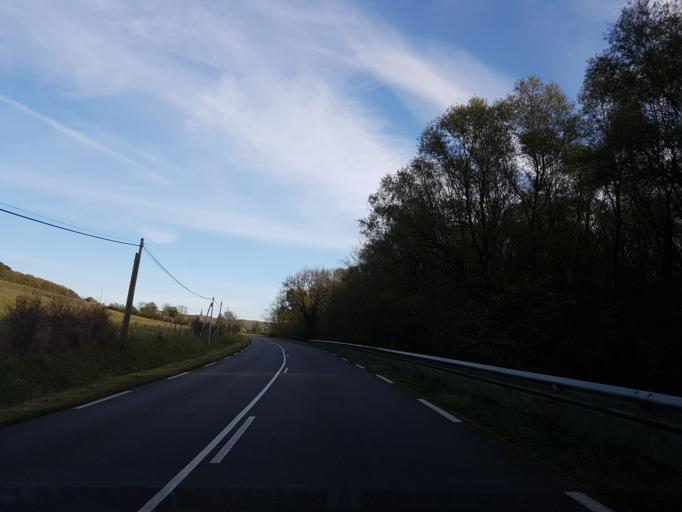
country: FR
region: Bourgogne
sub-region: Departement de la Cote-d'Or
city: Pouilly-en-Auxois
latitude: 47.3070
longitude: 4.6307
